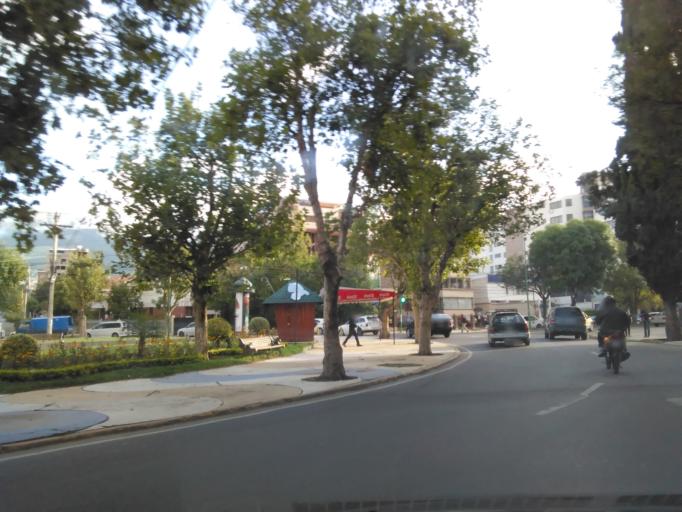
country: BO
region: Cochabamba
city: Cochabamba
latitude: -17.3732
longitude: -66.1569
